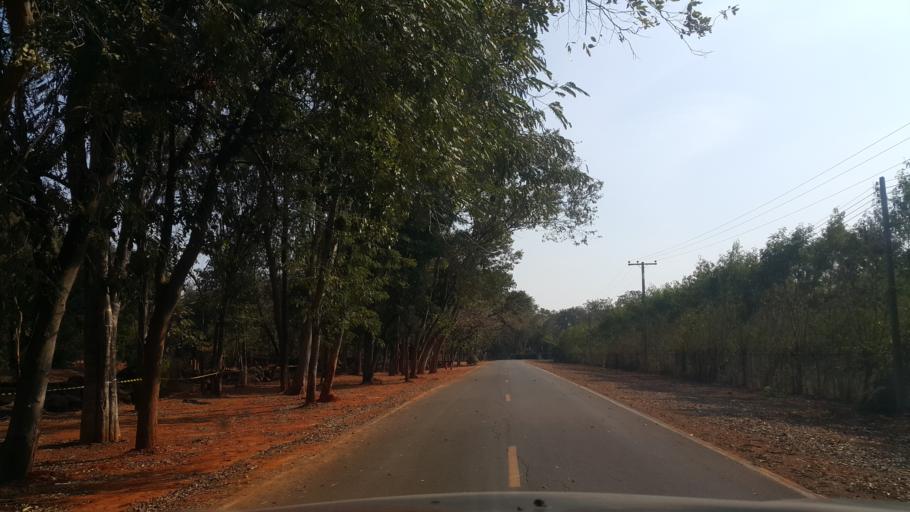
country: TH
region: Nakhon Ratchasima
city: Nakhon Ratchasima
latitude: 14.8558
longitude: 102.0857
